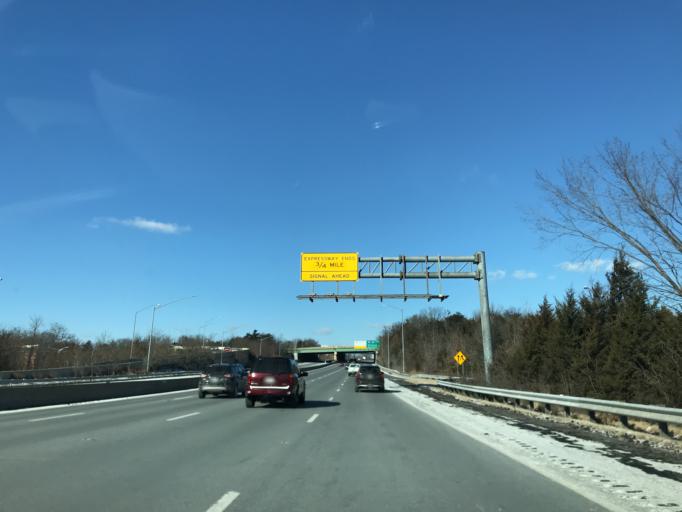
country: US
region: Maryland
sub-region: Prince George's County
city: Camp Springs
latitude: 38.8171
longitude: -76.9165
